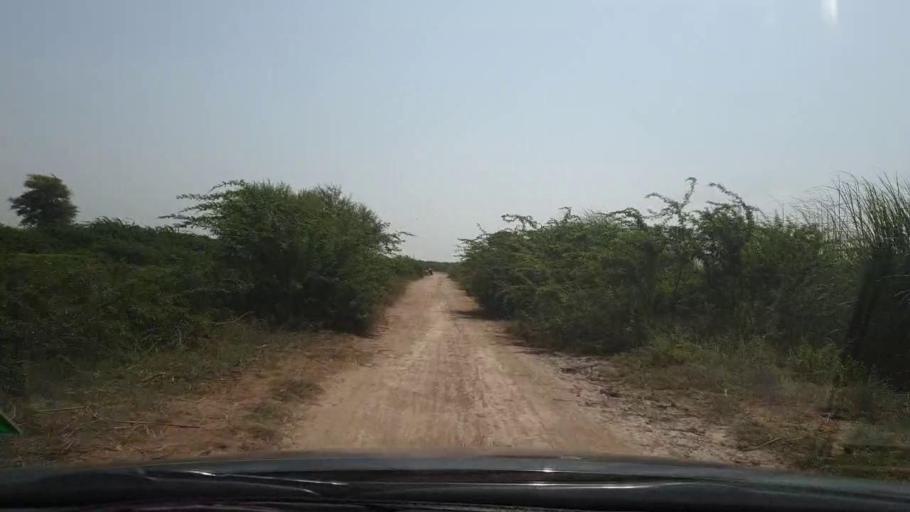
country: PK
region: Sindh
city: Tando Bago
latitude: 24.7885
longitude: 69.1184
